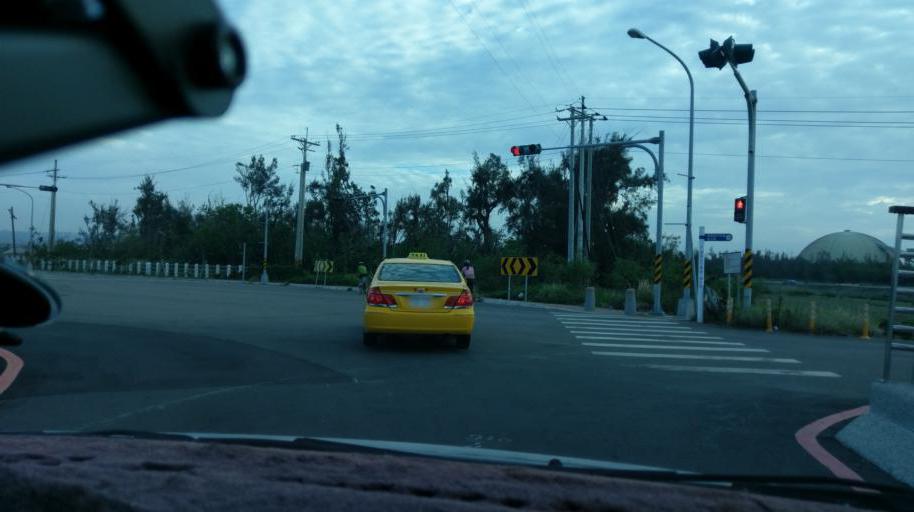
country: TW
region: Taiwan
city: Fengyuan
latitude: 24.2999
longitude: 120.5464
